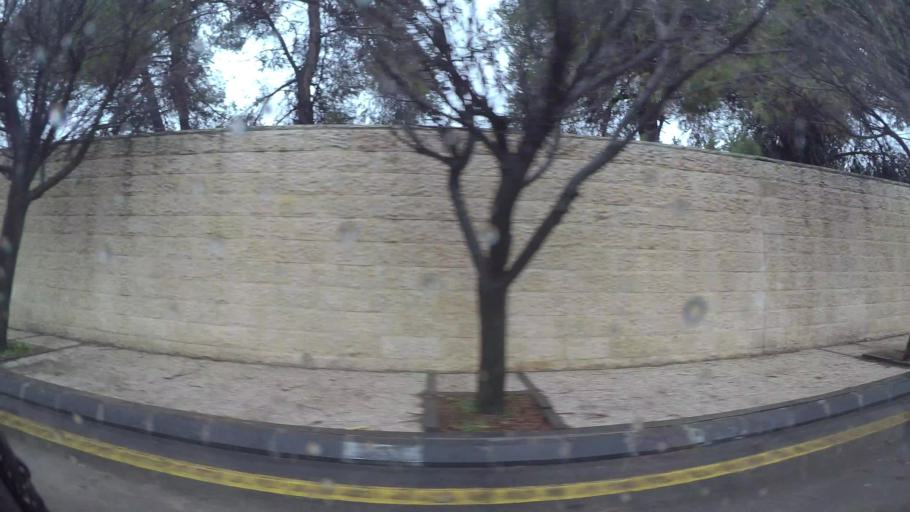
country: JO
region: Amman
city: Wadi as Sir
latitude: 31.9966
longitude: 35.8171
